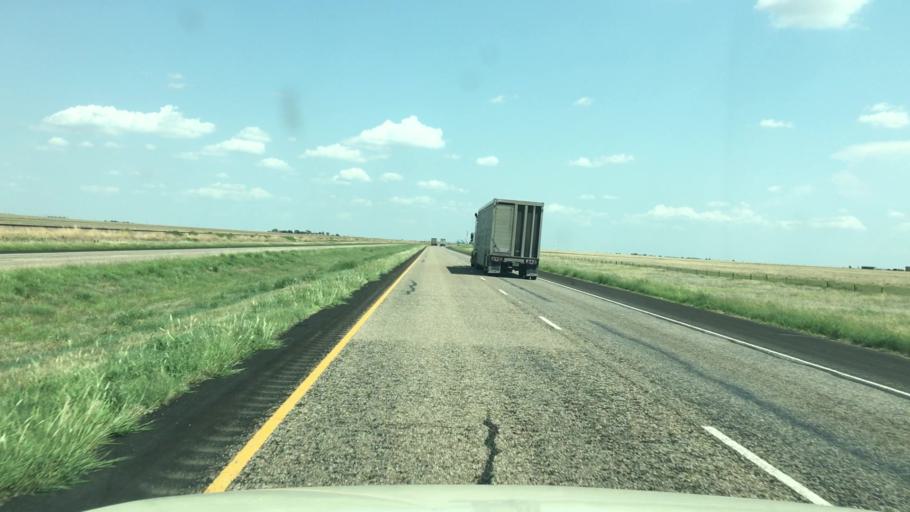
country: US
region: Texas
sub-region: Armstrong County
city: Claude
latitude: 35.1278
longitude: -101.4047
